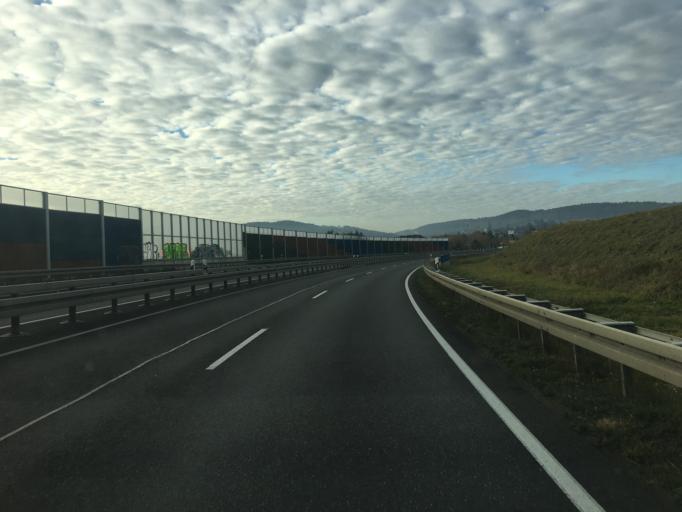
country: DE
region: North Rhine-Westphalia
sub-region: Regierungsbezirk Koln
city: Mechernich
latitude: 50.6209
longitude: 6.6642
